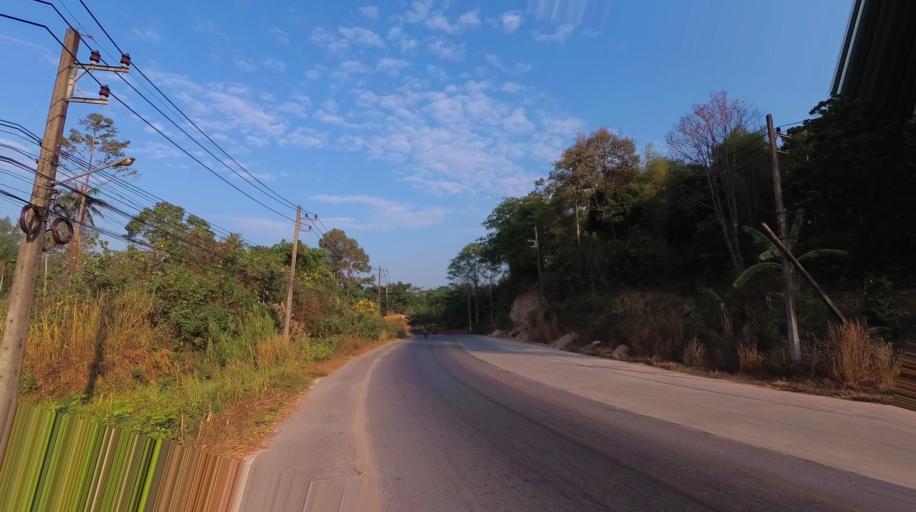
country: TH
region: Trat
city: Ko Chang Tai
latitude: 12.0636
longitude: 102.2873
